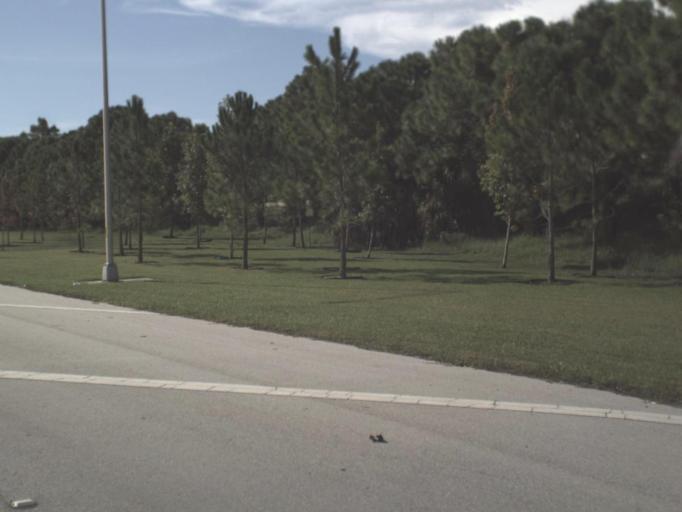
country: US
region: Florida
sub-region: Sarasota County
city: Laurel
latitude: 27.1483
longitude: -82.4634
